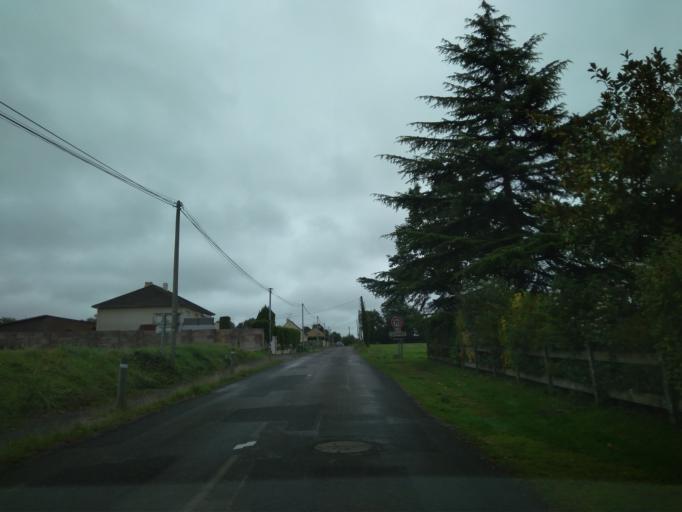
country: FR
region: Brittany
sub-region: Departement d'Ille-et-Vilaine
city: Betton
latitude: 48.1726
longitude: -1.6320
